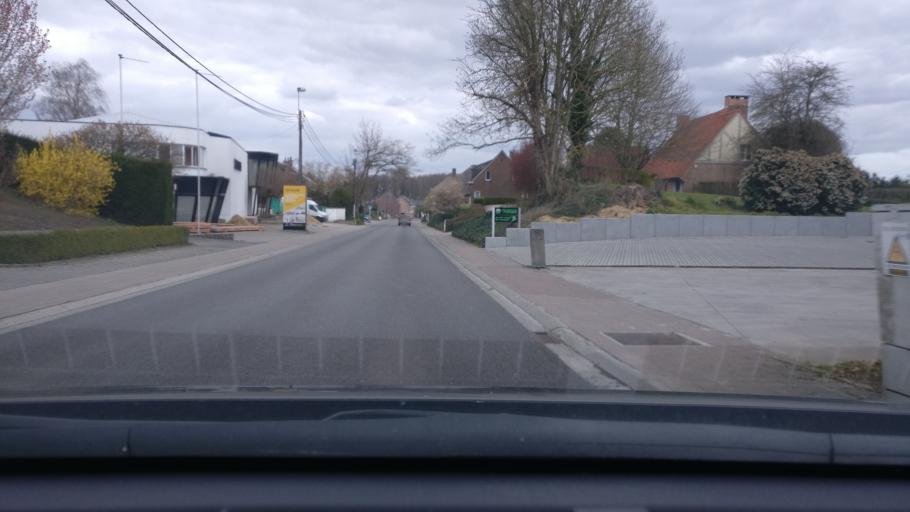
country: BE
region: Flanders
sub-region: Provincie Vlaams-Brabant
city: Overijse
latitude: 50.7941
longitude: 4.5436
